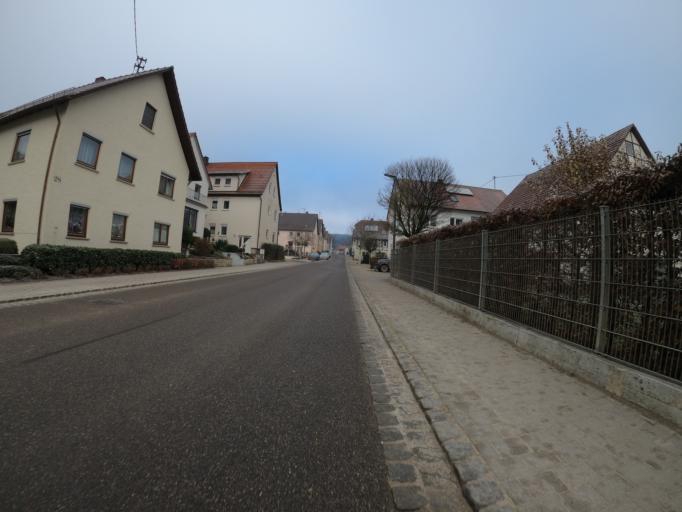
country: DE
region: Baden-Wuerttemberg
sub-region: Tuebingen Region
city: Westerstetten
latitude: 48.5199
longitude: 9.9525
